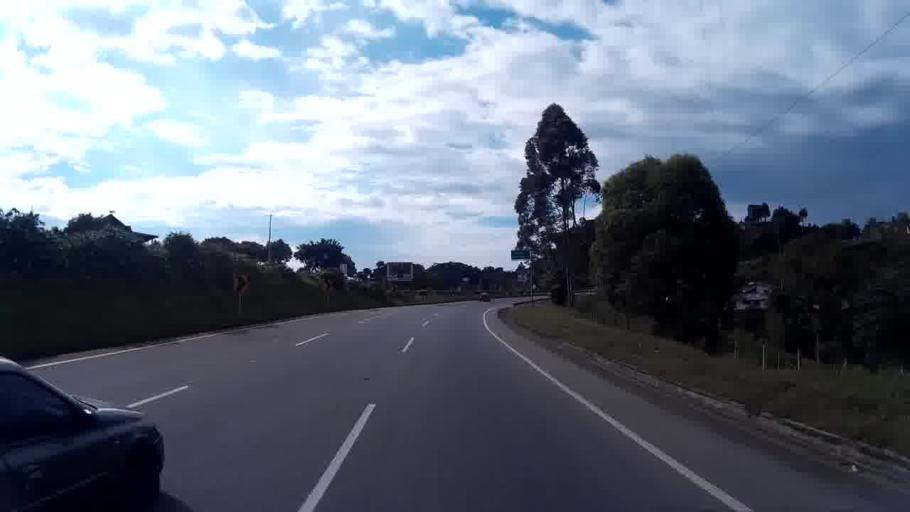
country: CO
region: Quindio
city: Circasia
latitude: 4.5943
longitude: -75.6409
